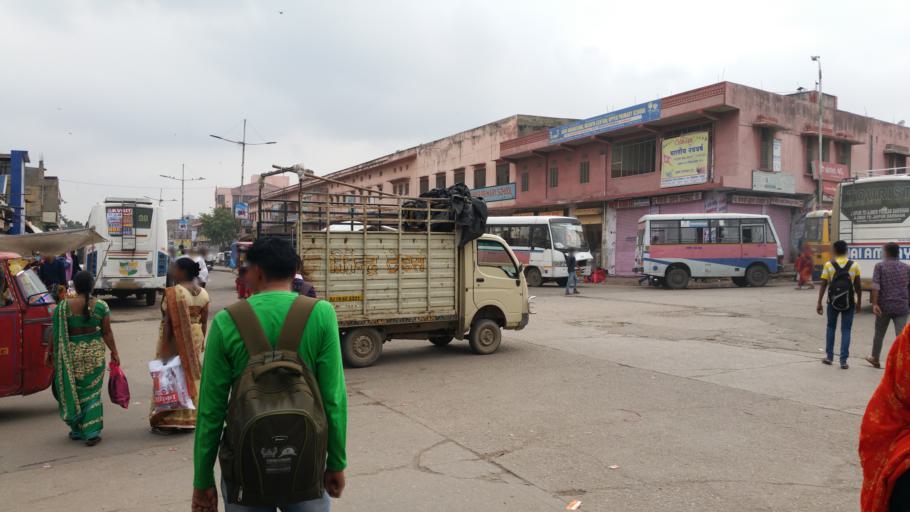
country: IN
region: Rajasthan
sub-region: Jaipur
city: Jaipur
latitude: 26.9259
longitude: 75.8079
